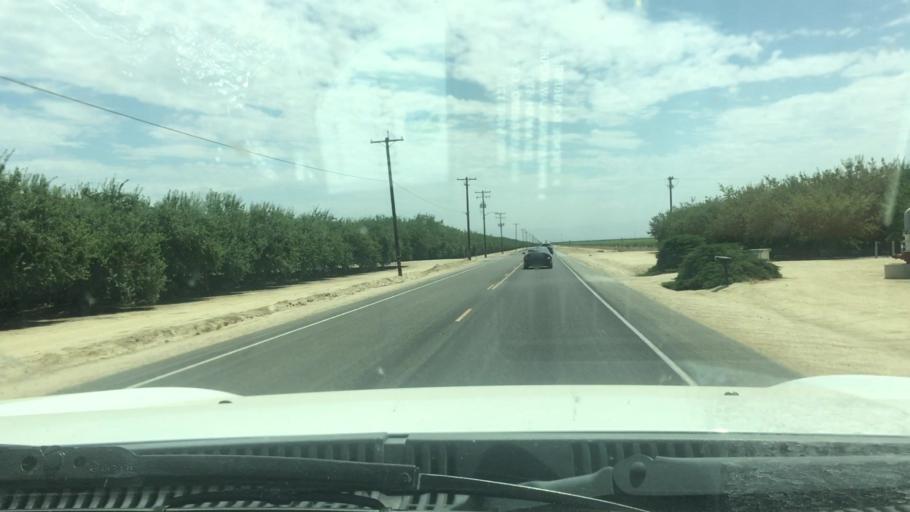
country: US
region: California
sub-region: Kern County
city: Wasco
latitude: 35.5580
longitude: -119.3144
